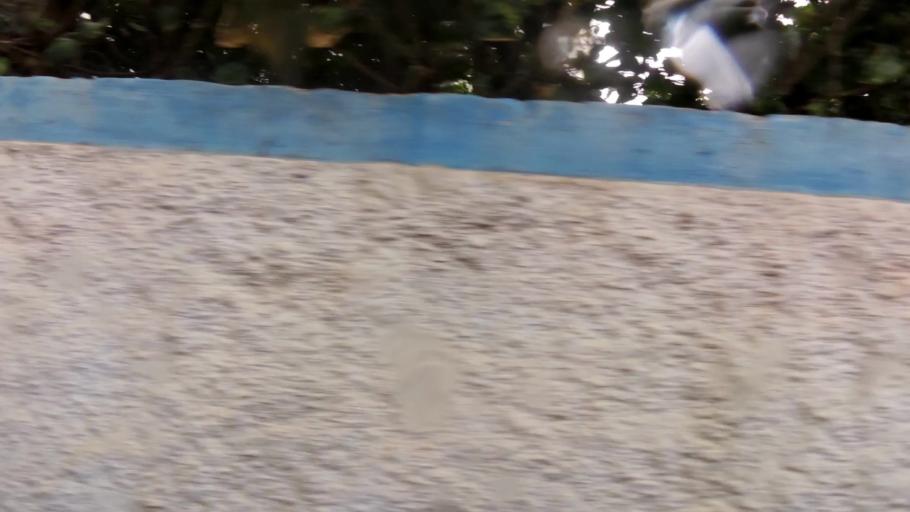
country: MA
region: Tanger-Tetouan
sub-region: Tetouan
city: Martil
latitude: 35.6237
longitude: -5.2746
